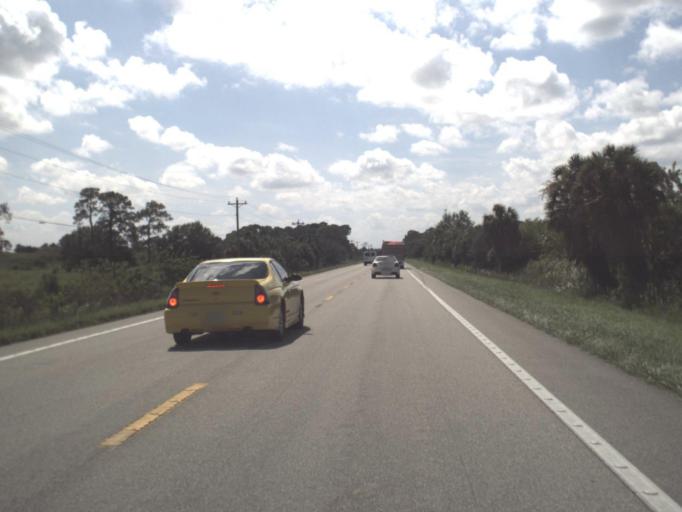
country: US
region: Florida
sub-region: Collier County
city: Immokalee
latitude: 26.5732
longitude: -81.4363
